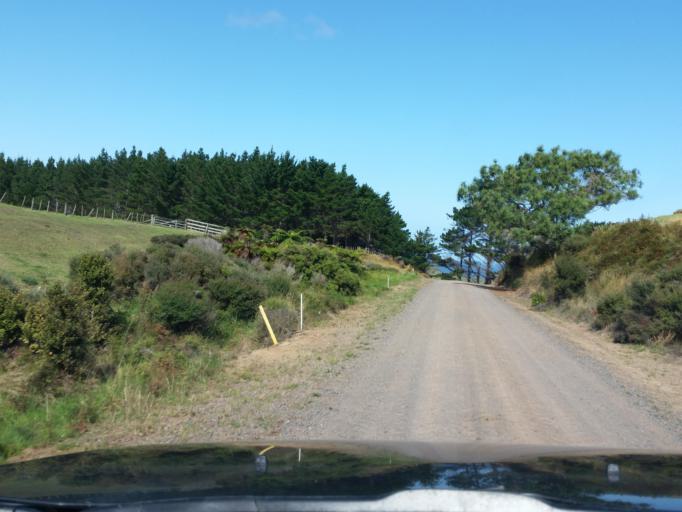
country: NZ
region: Northland
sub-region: Kaipara District
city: Dargaville
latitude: -35.7006
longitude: 173.5229
